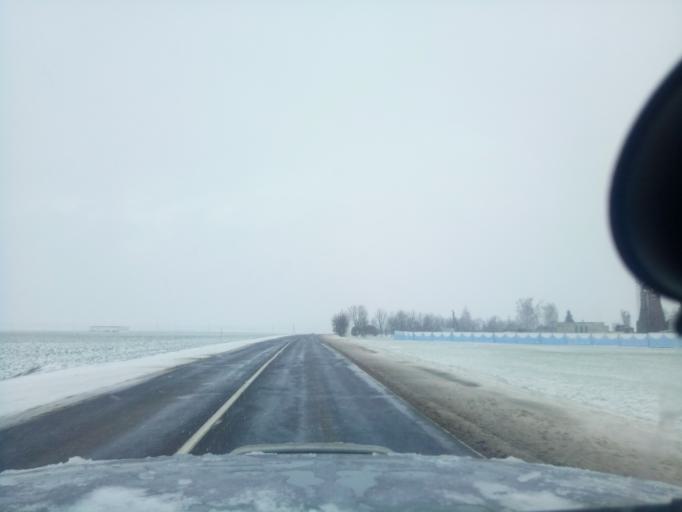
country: BY
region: Minsk
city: Haradzyeya
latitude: 53.3199
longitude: 26.5583
